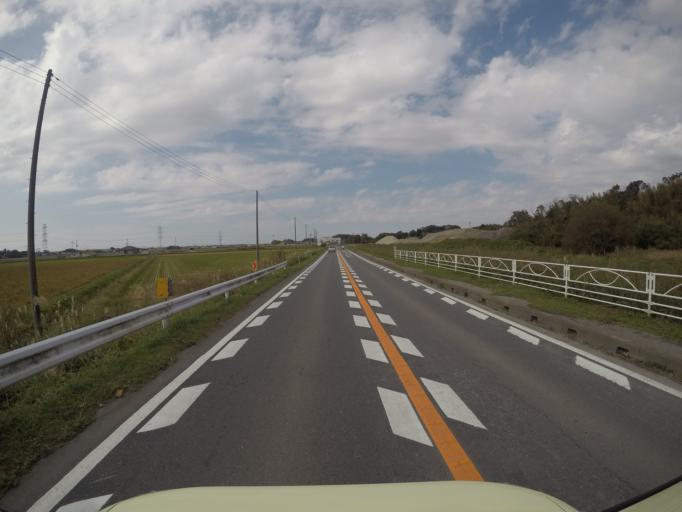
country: JP
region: Ibaraki
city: Iwai
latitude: 35.9891
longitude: 139.9100
